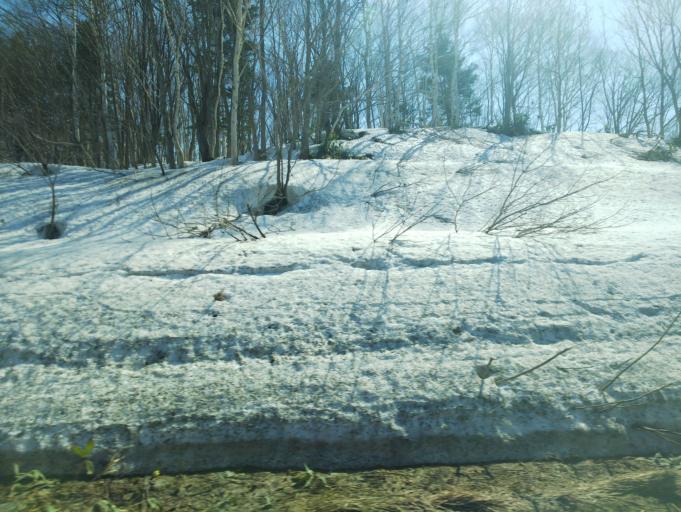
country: JP
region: Hokkaido
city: Nayoro
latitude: 44.7011
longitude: 142.2733
